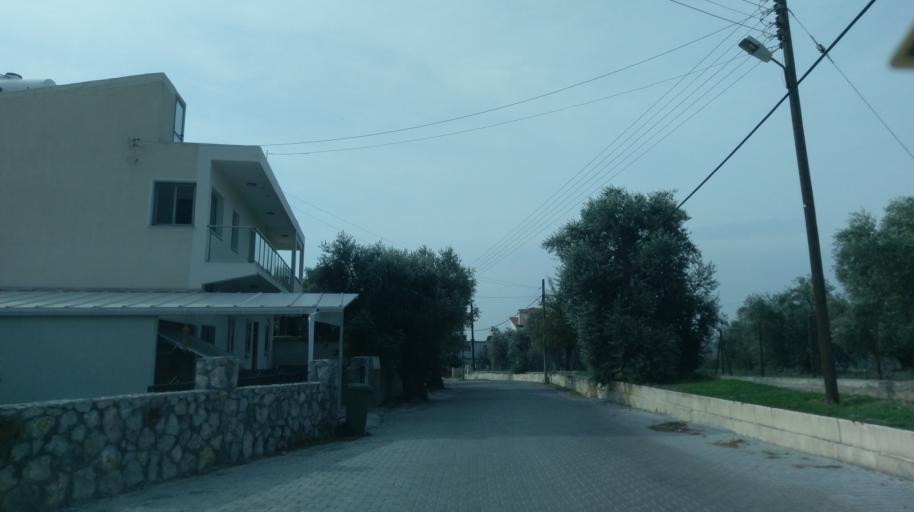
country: CY
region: Keryneia
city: Lapithos
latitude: 35.3070
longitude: 33.1381
